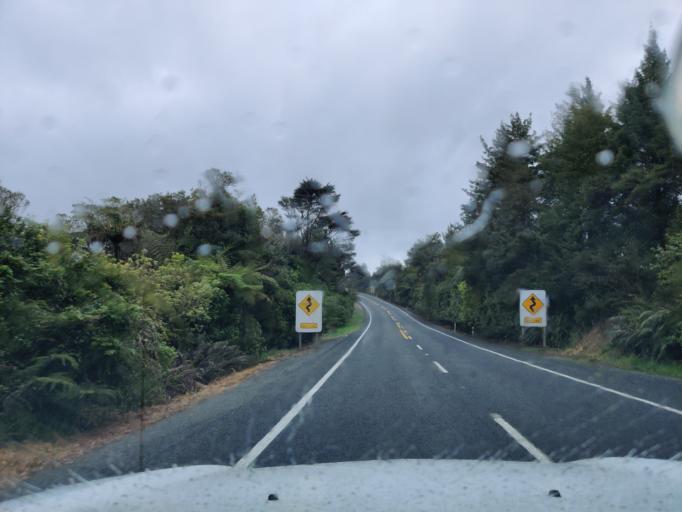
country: NZ
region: Waikato
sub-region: South Waikato District
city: Tokoroa
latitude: -38.0083
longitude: 175.9297
